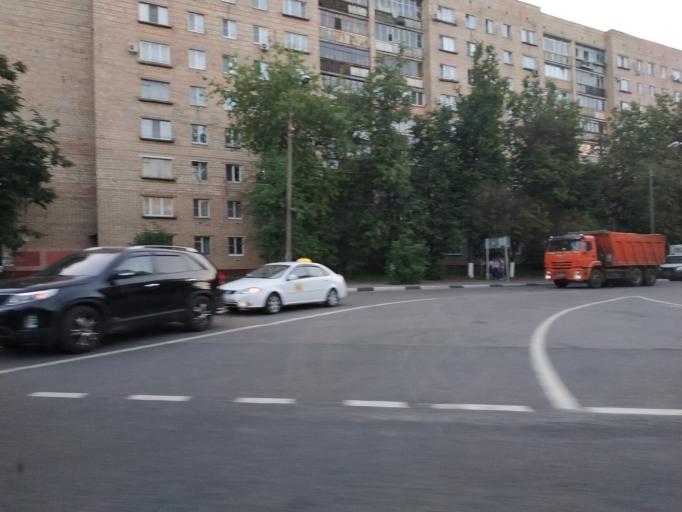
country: RU
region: Moskovskaya
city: Fryazino
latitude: 55.9529
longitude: 38.0529
